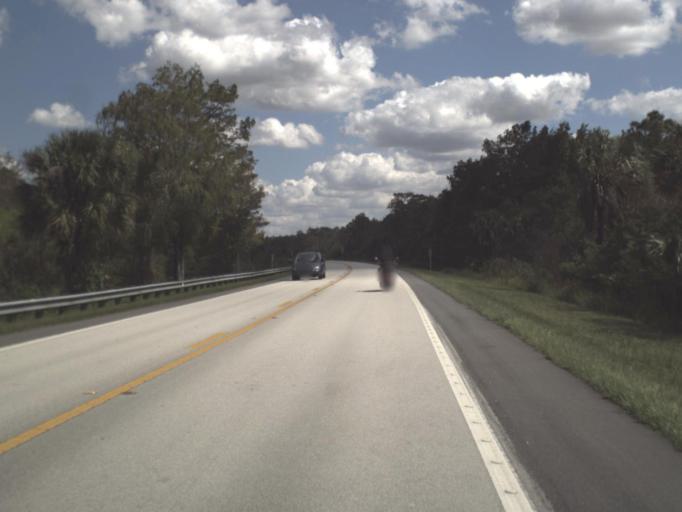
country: US
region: Florida
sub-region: Collier County
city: Marco
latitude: 25.8791
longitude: -81.2426
